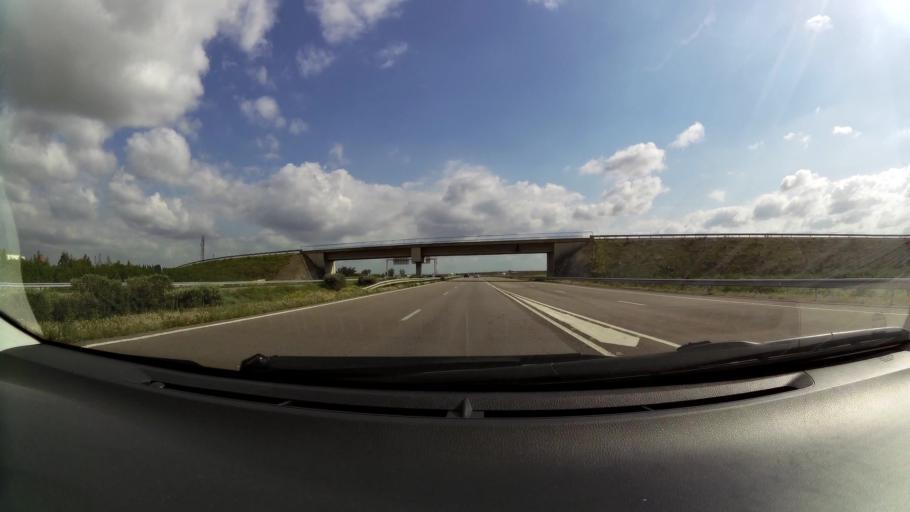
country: MA
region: Chaouia-Ouardigha
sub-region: Settat Province
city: Berrechid
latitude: 33.2802
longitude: -7.5472
